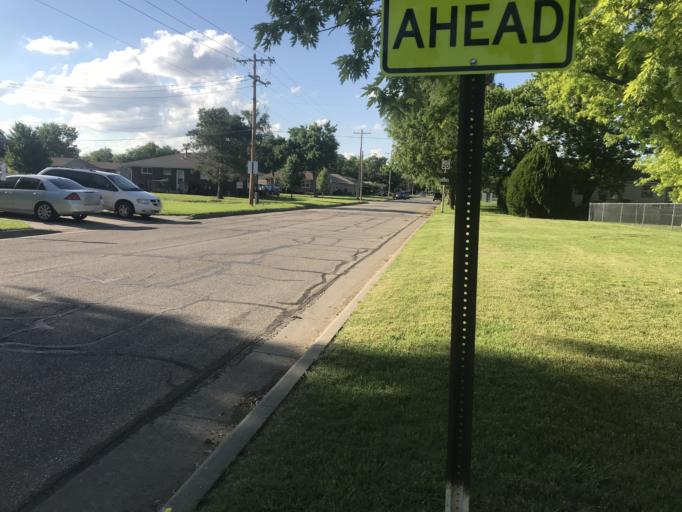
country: US
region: Kansas
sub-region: Saline County
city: Salina
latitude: 38.8154
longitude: -97.6028
